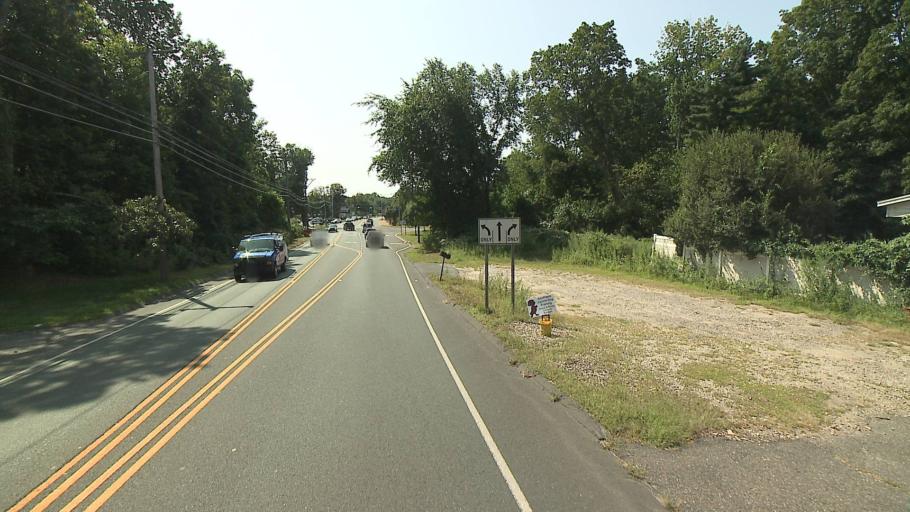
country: US
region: Connecticut
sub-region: Fairfield County
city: Newtown
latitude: 41.3496
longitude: -73.2602
